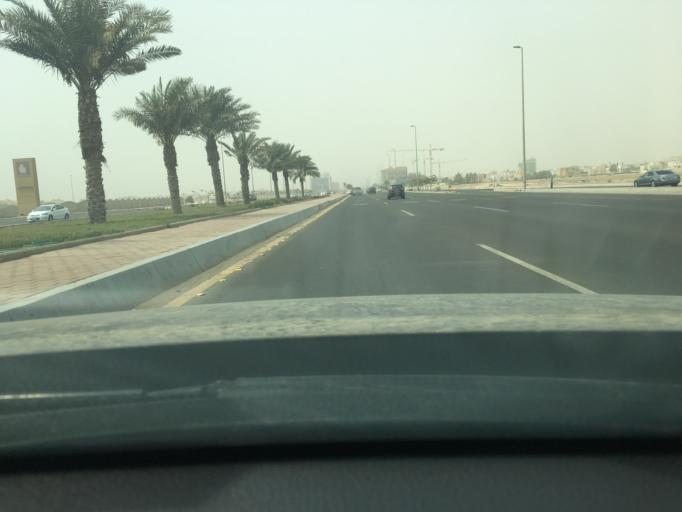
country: SA
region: Makkah
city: Jeddah
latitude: 21.6376
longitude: 39.1120
